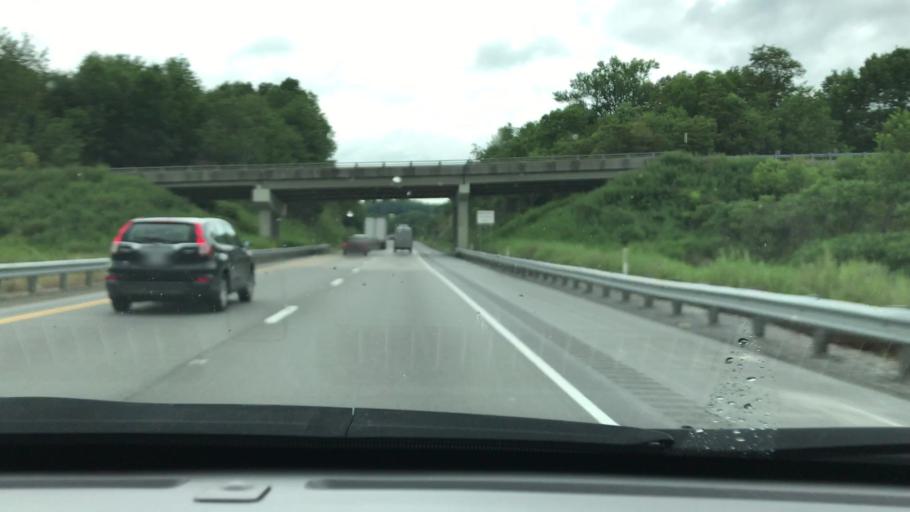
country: US
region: Pennsylvania
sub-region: Clearfield County
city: Clearfield
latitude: 41.0518
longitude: -78.4275
